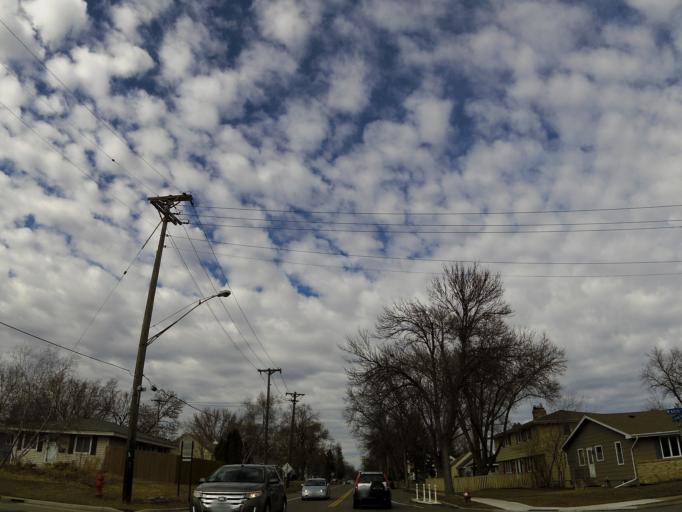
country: US
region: Minnesota
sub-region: Hennepin County
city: Edina
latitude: 44.8942
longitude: -93.3189
